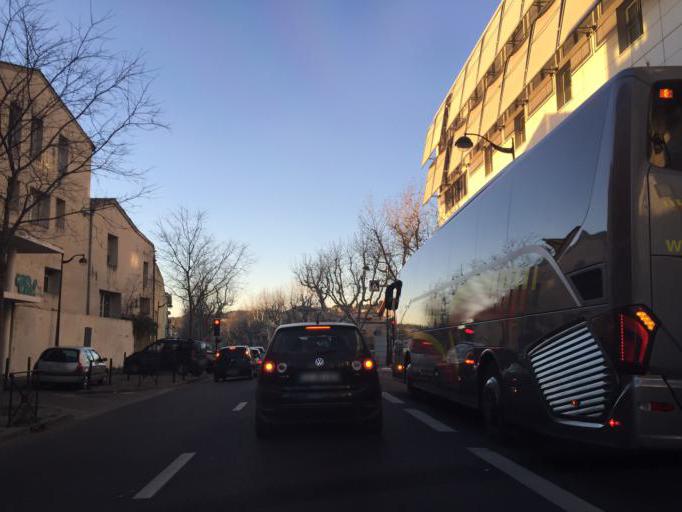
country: FR
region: Provence-Alpes-Cote d'Azur
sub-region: Departement des Bouches-du-Rhone
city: Aix-en-Provence
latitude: 43.5282
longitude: 5.4549
